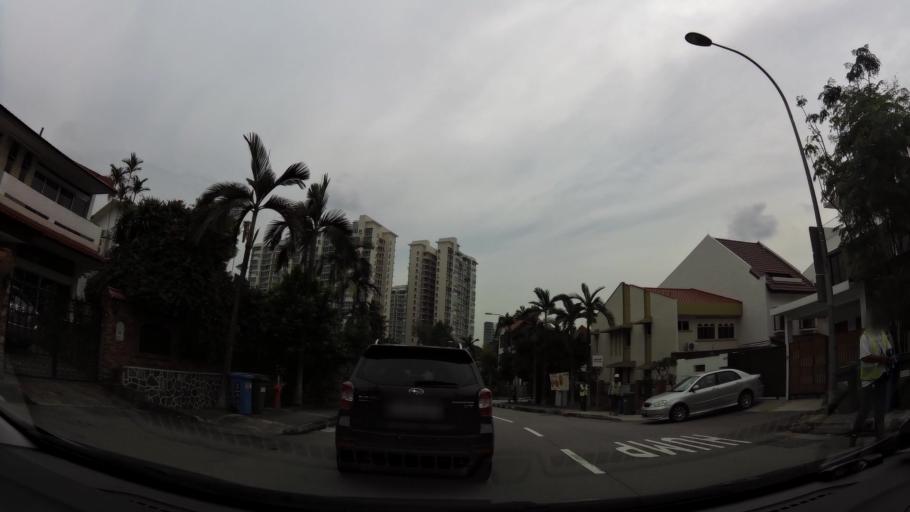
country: SG
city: Singapore
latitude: 1.3550
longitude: 103.8629
